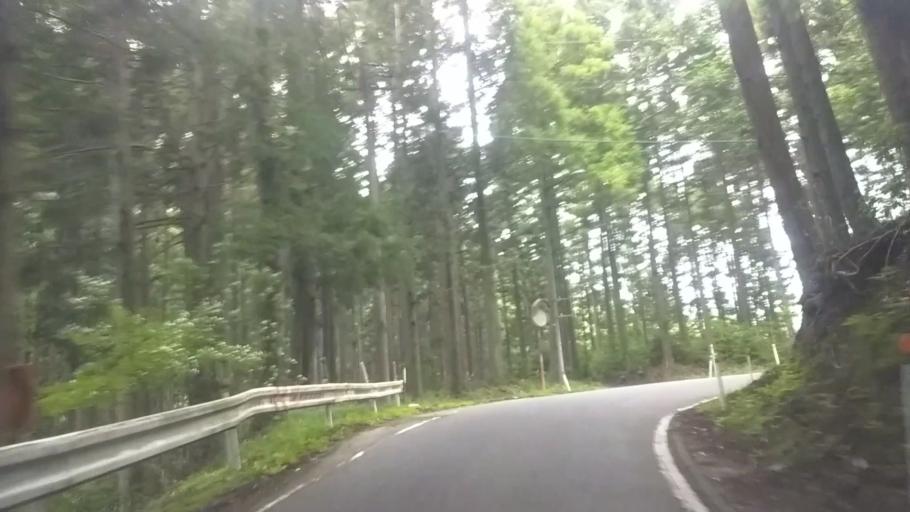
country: JP
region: Chiba
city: Kawaguchi
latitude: 35.1899
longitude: 140.1385
